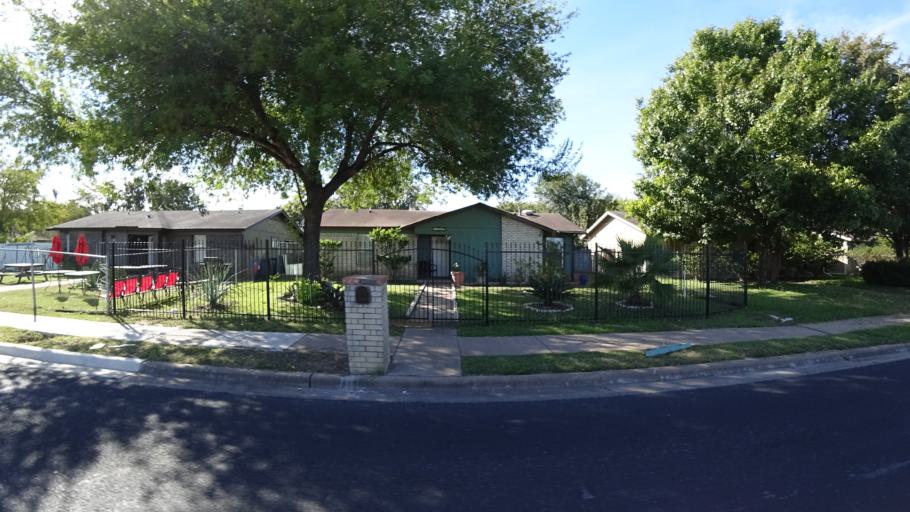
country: US
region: Texas
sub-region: Travis County
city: Onion Creek
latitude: 30.1897
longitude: -97.7452
